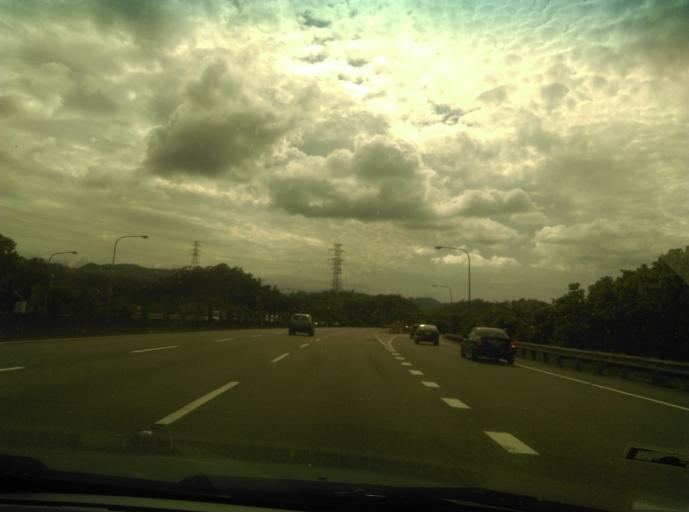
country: TW
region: Taipei
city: Taipei
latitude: 25.0595
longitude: 121.6410
